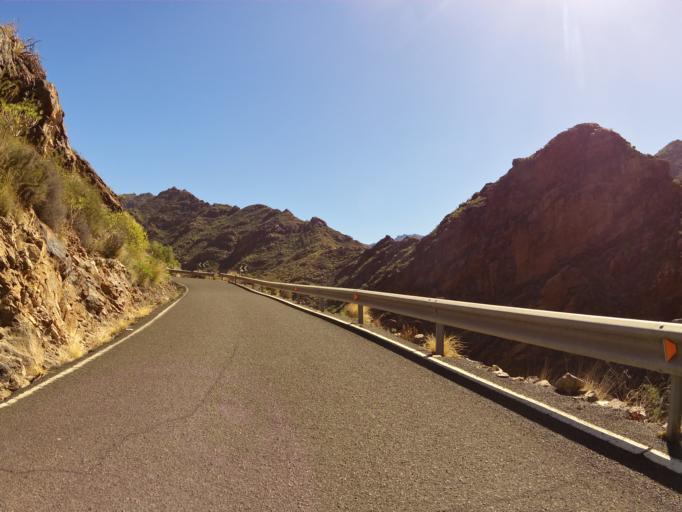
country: ES
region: Canary Islands
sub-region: Provincia de Las Palmas
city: Artenara
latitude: 27.9930
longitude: -15.6868
